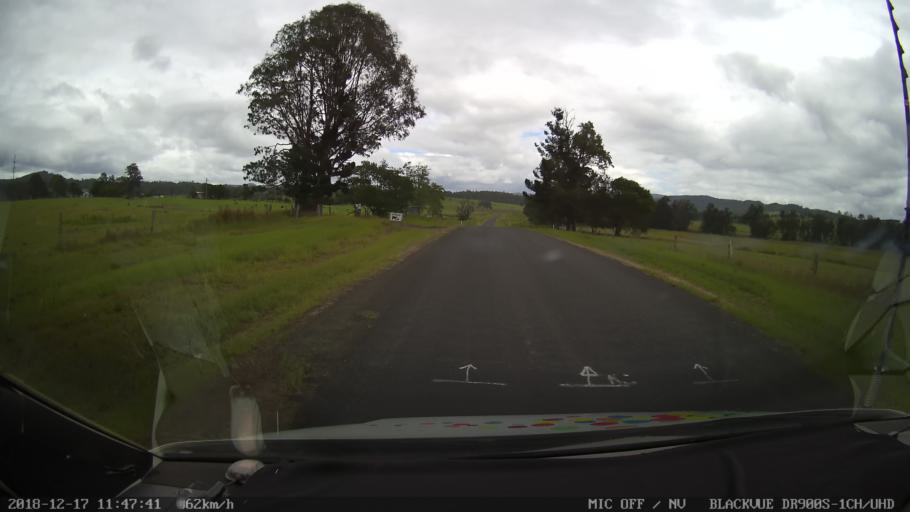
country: AU
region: New South Wales
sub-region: Kyogle
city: Kyogle
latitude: -28.6249
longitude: 152.5910
